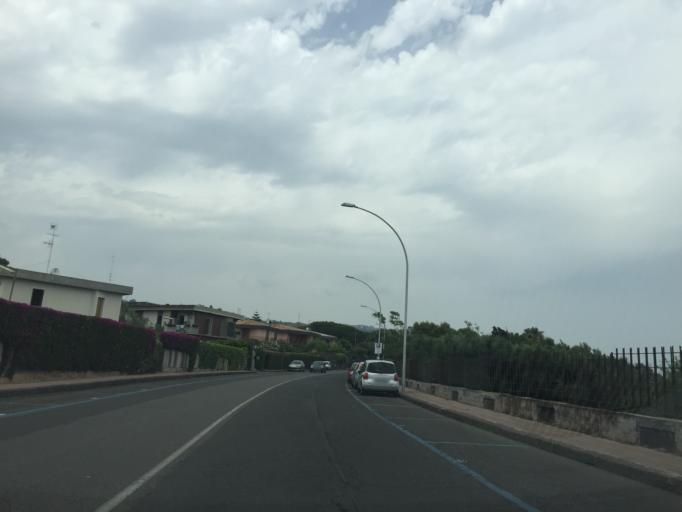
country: IT
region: Sicily
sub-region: Catania
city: Aci Castello
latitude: 37.5474
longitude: 15.1439
